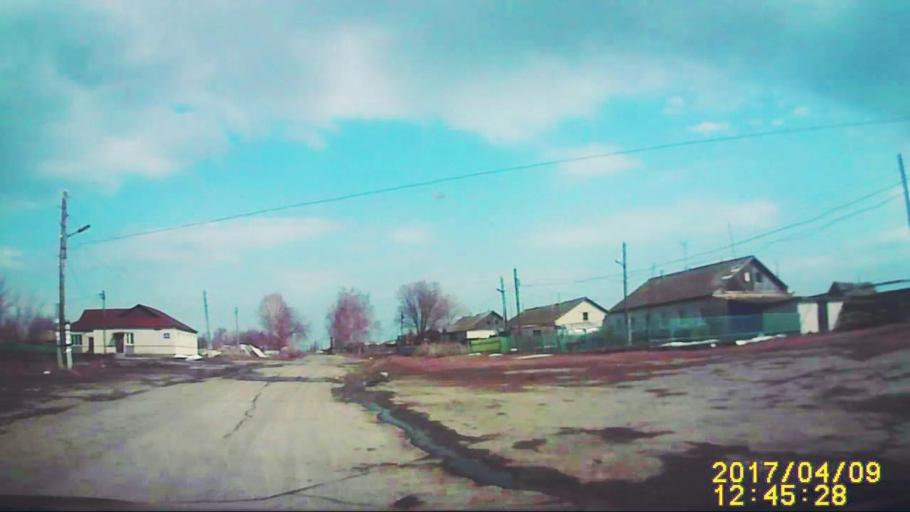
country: RU
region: Ulyanovsk
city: Ignatovka
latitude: 54.0111
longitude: 47.9183
